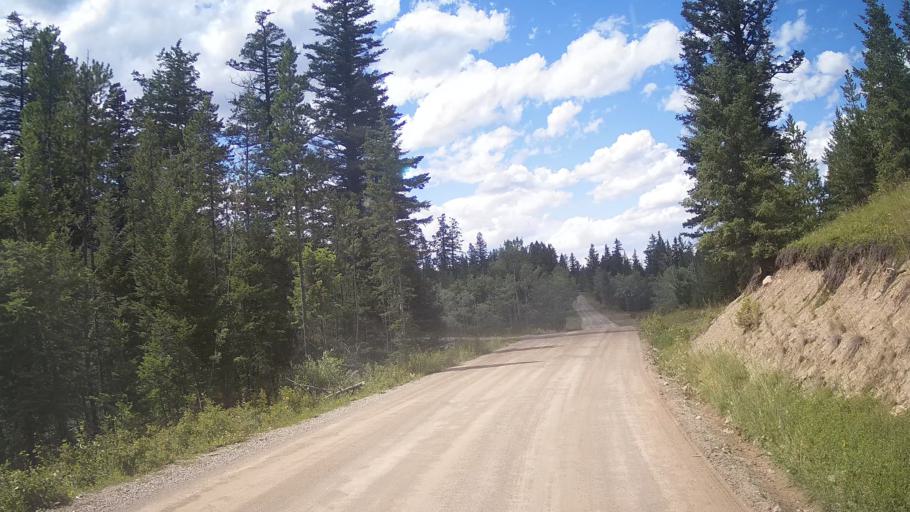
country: CA
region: British Columbia
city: Lillooet
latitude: 51.3104
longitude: -121.8443
